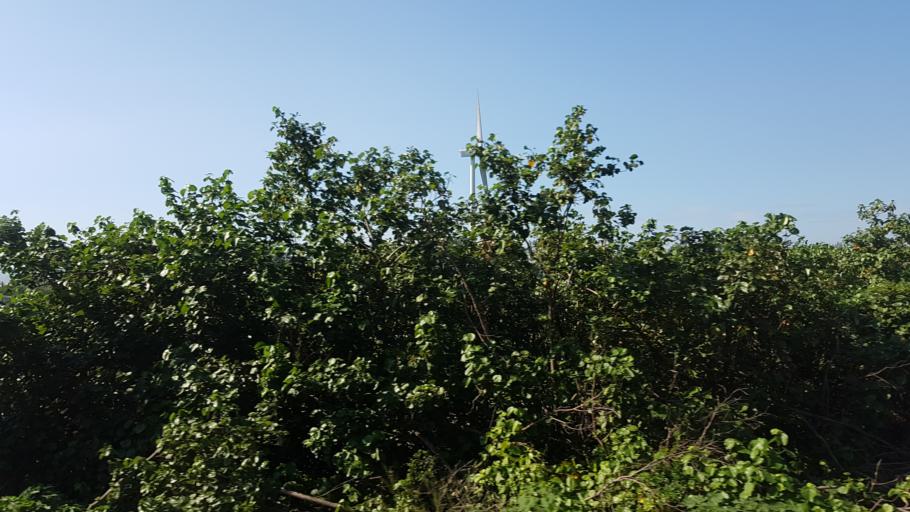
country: TW
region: Taiwan
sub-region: Hsinchu
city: Hsinchu
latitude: 24.7322
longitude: 120.8824
